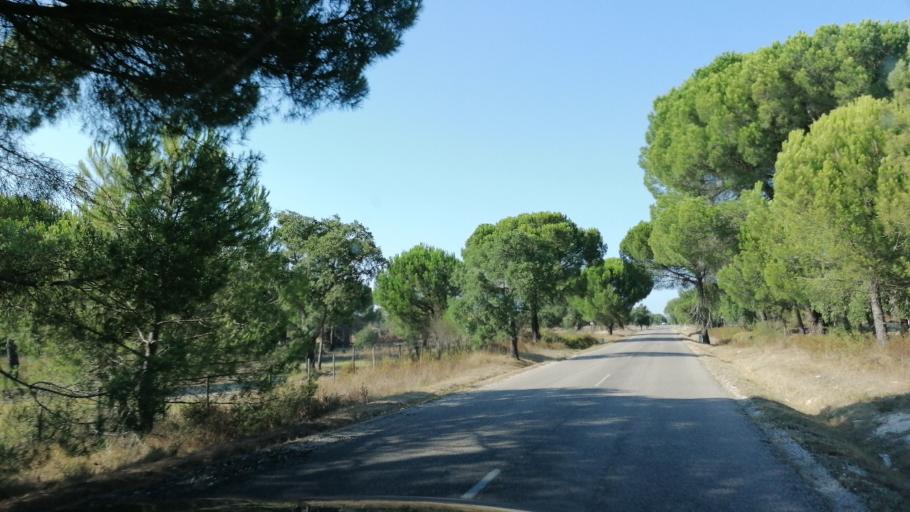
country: PT
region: Santarem
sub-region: Coruche
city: Coruche
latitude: 38.9113
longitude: -8.5260
